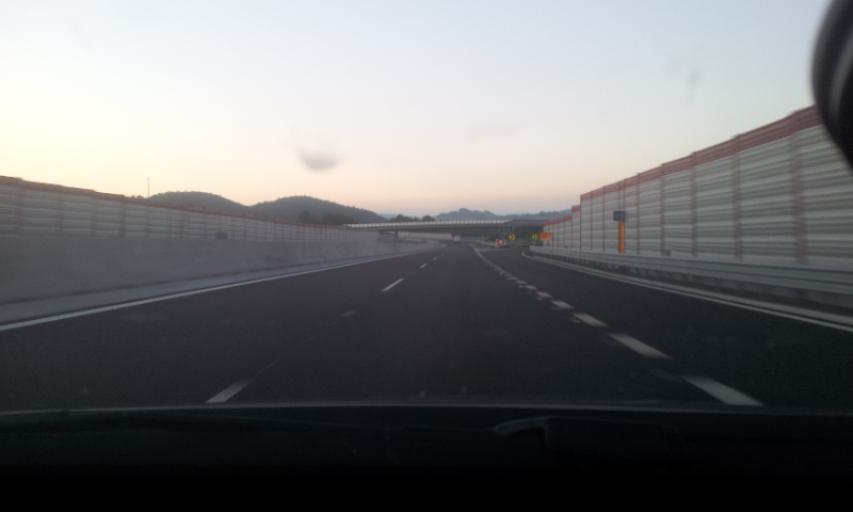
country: SK
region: Banskobystricky
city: Detva
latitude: 48.5394
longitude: 19.3957
